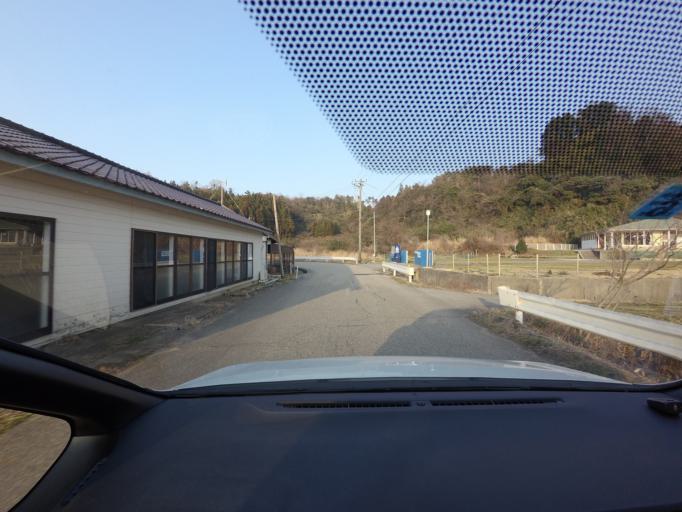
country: JP
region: Ishikawa
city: Nanao
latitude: 37.1418
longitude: 137.0153
